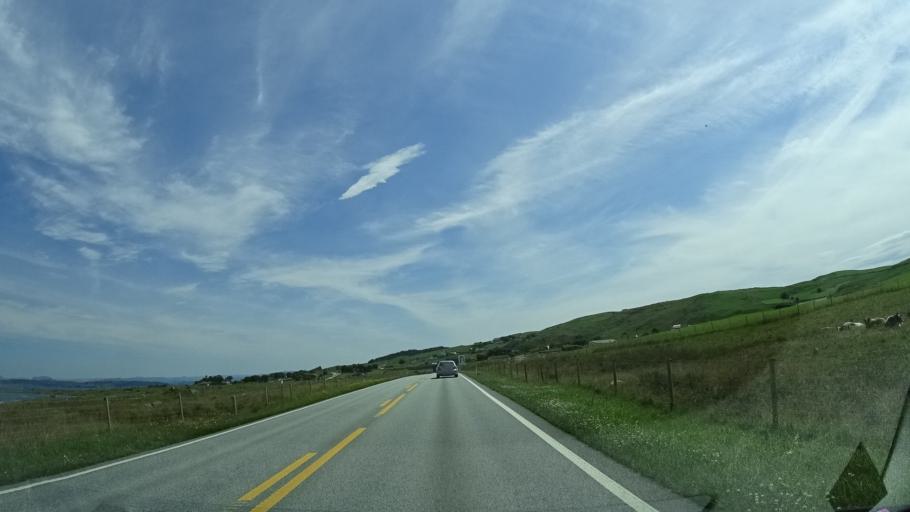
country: NO
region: Rogaland
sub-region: Rennesoy
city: Vikevag
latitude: 59.1283
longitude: 5.6192
